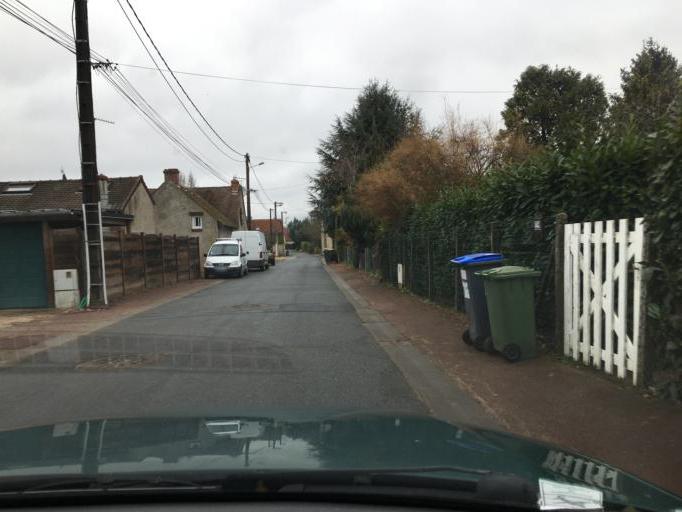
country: FR
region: Centre
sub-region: Departement du Loiret
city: Saint-Pryve-Saint-Mesmin
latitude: 47.8639
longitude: 1.8758
